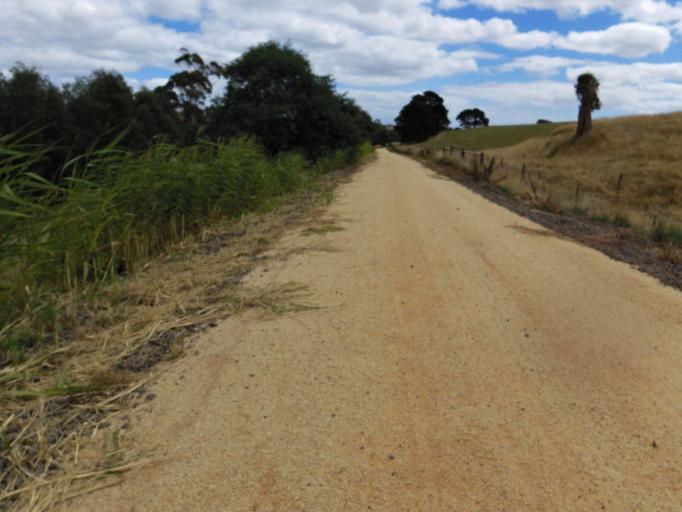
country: AU
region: Victoria
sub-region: Bass Coast
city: North Wonthaggi
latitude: -38.4165
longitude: 145.7446
